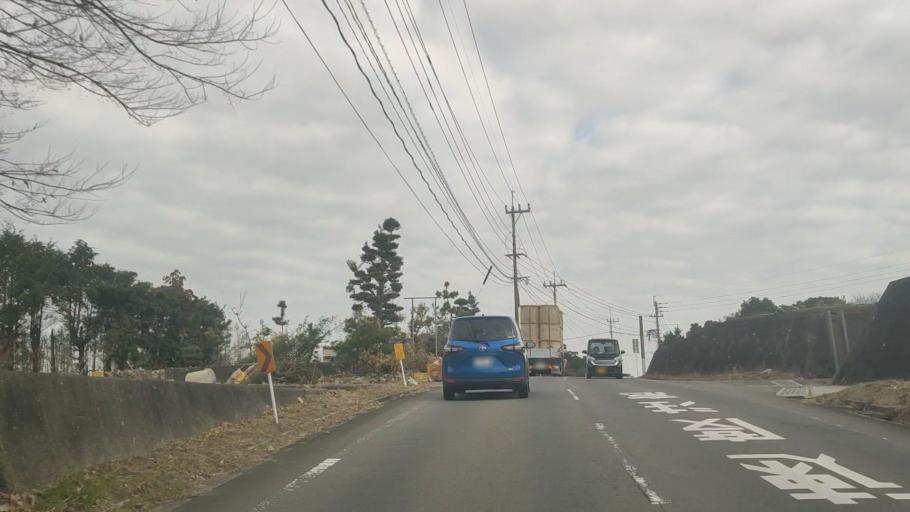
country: JP
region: Nagasaki
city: Shimabara
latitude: 32.8465
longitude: 130.2166
